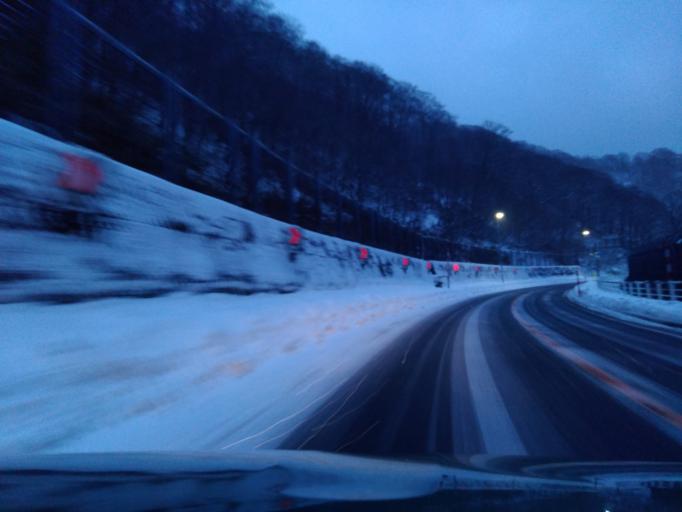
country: JP
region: Iwate
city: Shizukuishi
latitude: 39.7186
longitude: 140.8213
